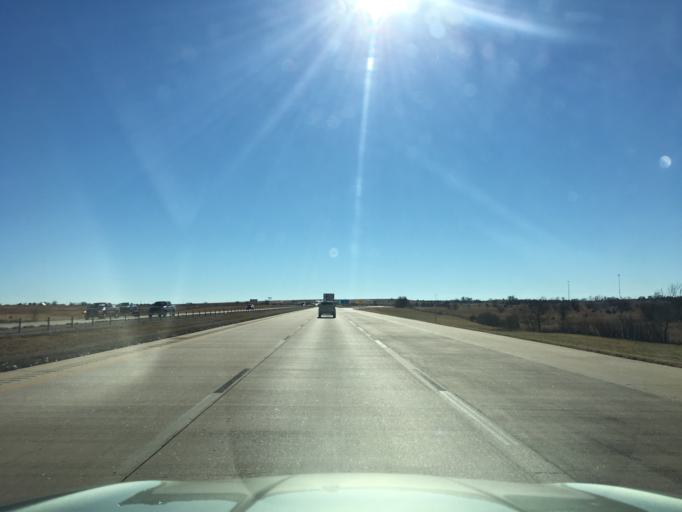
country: US
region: Oklahoma
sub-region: Noble County
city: Perry
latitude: 36.4177
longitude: -97.3272
